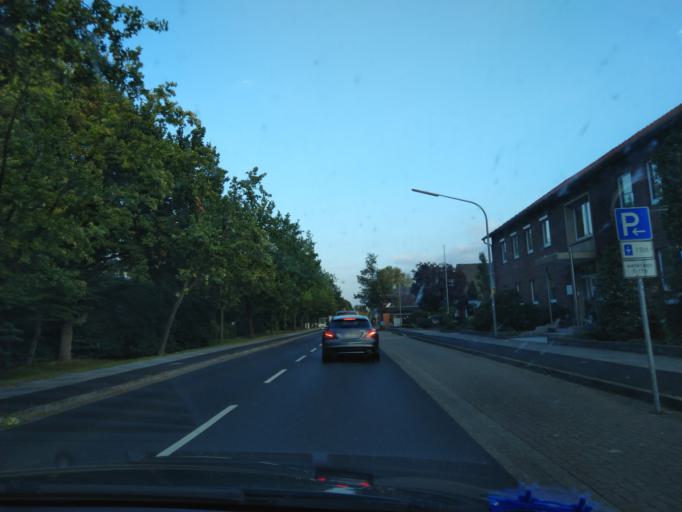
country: DE
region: Lower Saxony
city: Papenburg
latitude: 53.0757
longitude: 7.4080
